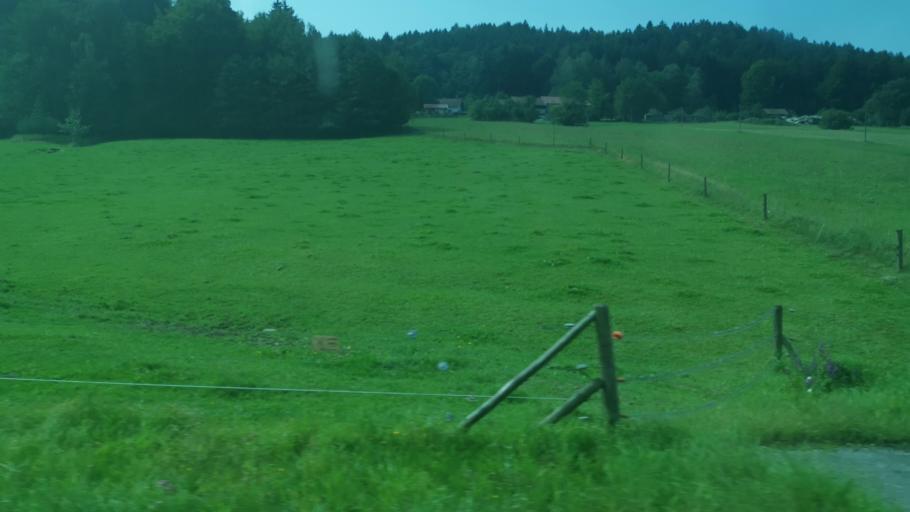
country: DE
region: Bavaria
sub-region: Upper Palatinate
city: Chamerau
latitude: 49.1848
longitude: 12.7415
